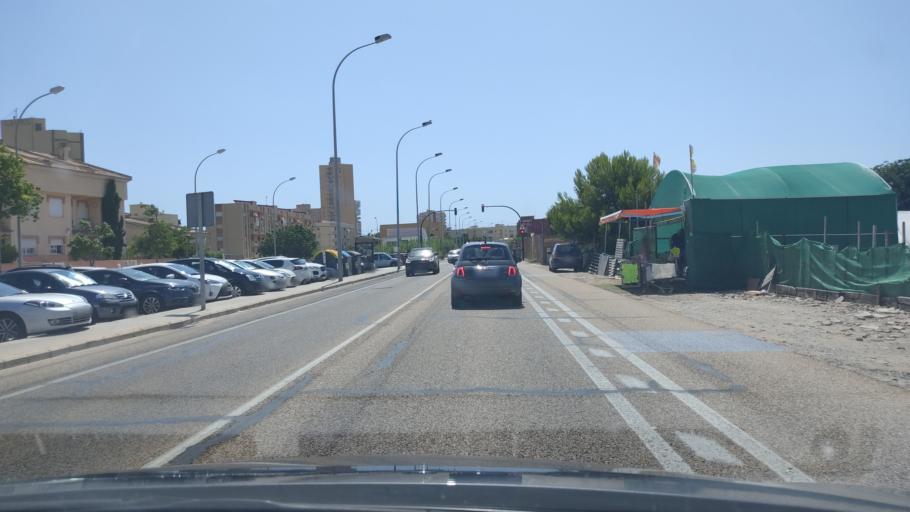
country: ES
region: Valencia
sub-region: Provincia de Valencia
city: Sollana
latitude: 39.3056
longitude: -0.2950
